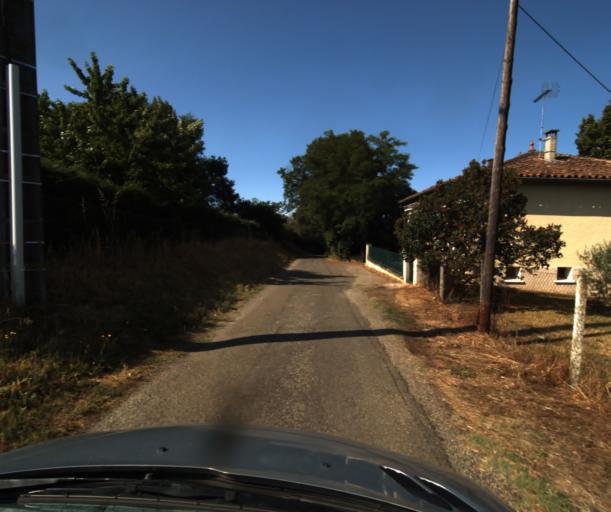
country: FR
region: Midi-Pyrenees
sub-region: Departement du Tarn-et-Garonne
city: Finhan
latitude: 43.9141
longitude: 1.2657
